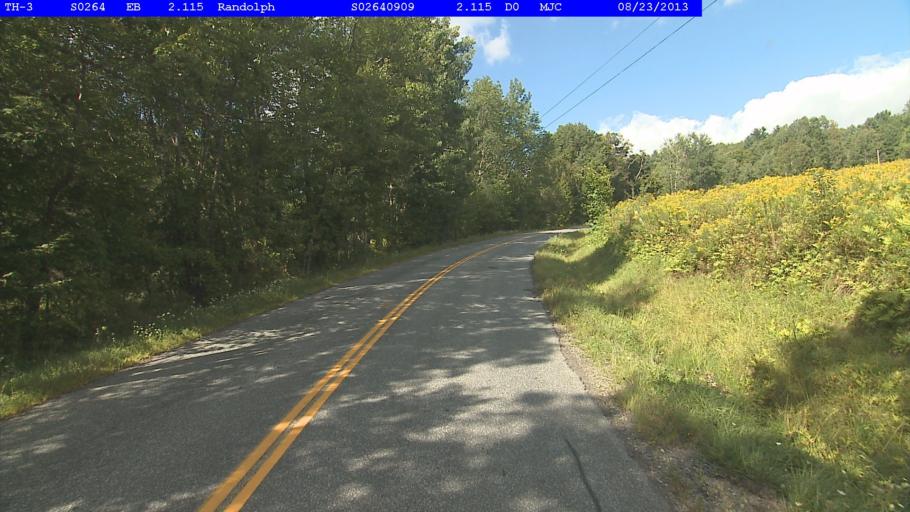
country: US
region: Vermont
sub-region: Orange County
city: Chelsea
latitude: 43.9569
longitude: -72.5314
